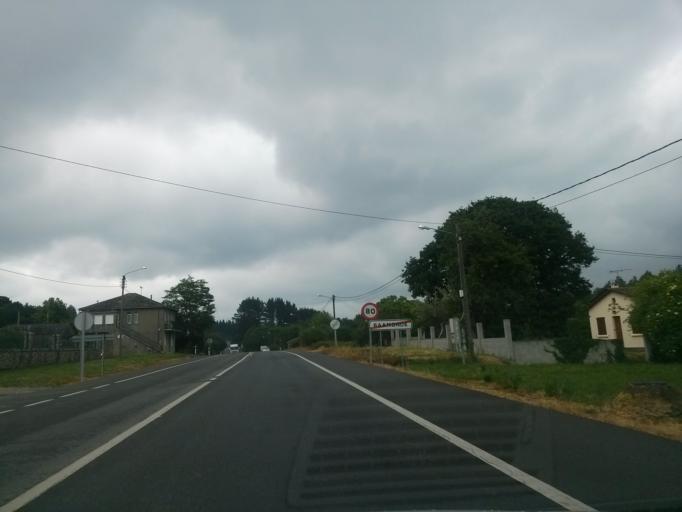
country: ES
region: Galicia
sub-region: Provincia de Lugo
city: Begonte
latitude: 43.1740
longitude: -7.7538
